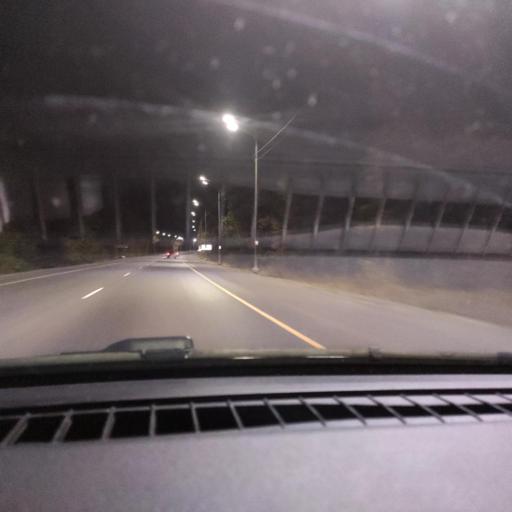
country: RU
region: Voronezj
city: Devitsa
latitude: 51.6348
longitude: 38.9992
